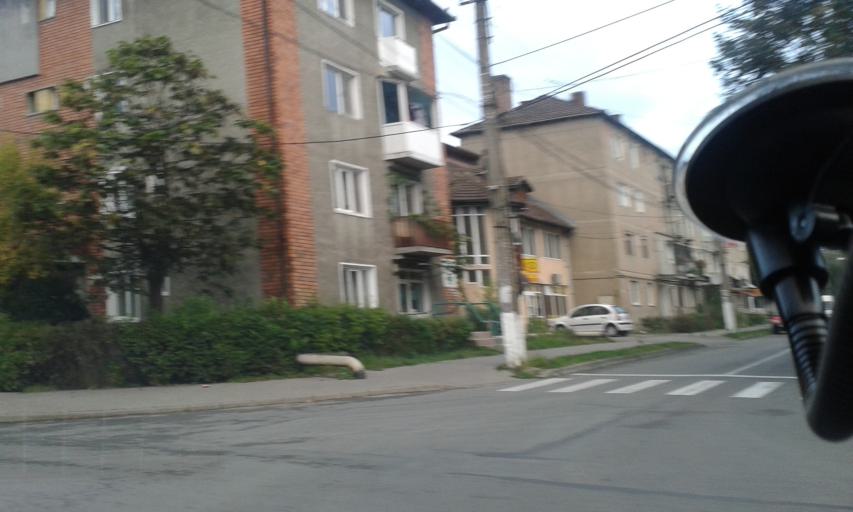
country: RO
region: Hunedoara
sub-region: Municipiul Petrosani
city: Petrosani
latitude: 45.3980
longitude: 23.3749
